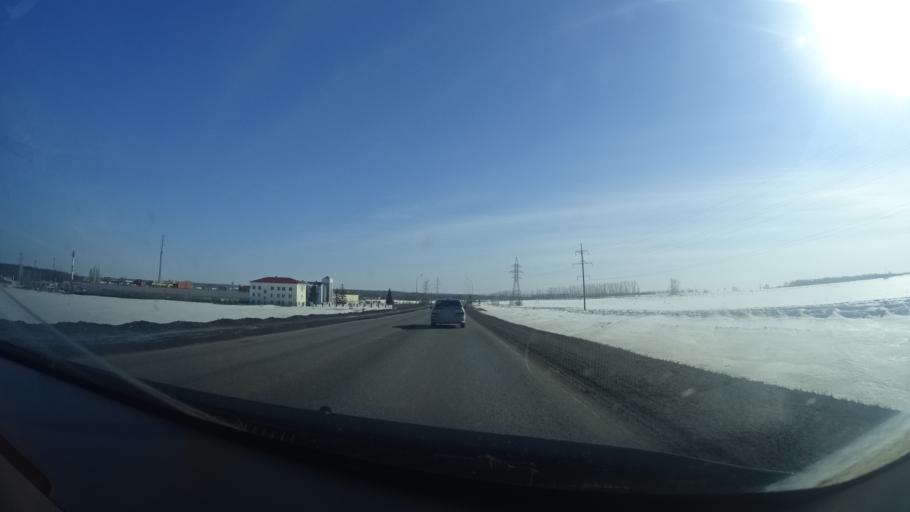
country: RU
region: Bashkortostan
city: Mikhaylovka
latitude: 54.8337
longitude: 55.8103
